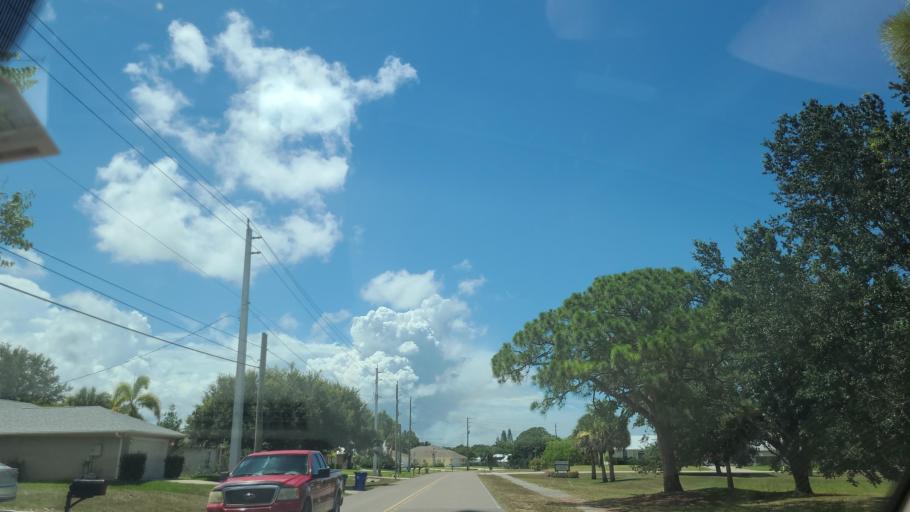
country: US
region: Florida
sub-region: Indian River County
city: Sebastian
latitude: 27.7635
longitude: -80.4649
